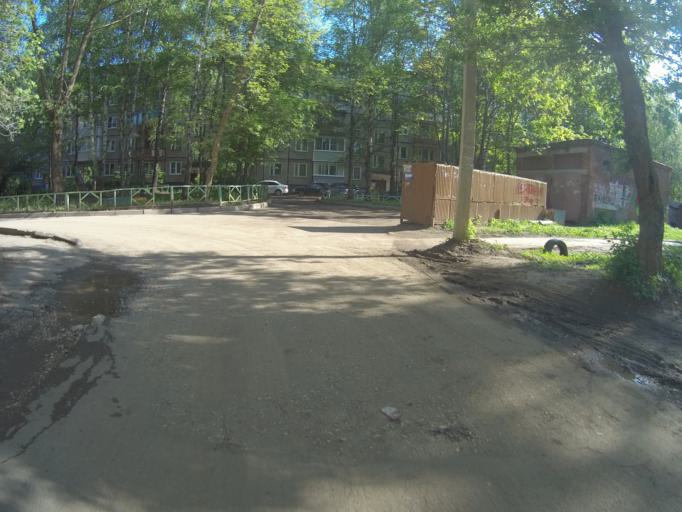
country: RU
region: Vladimir
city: Bogolyubovo
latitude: 56.1732
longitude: 40.4822
